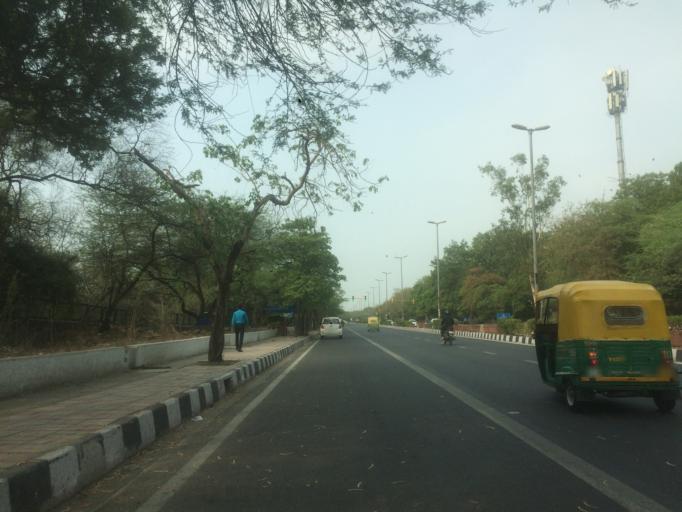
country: IN
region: NCT
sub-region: New Delhi
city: New Delhi
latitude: 28.5405
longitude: 77.1757
